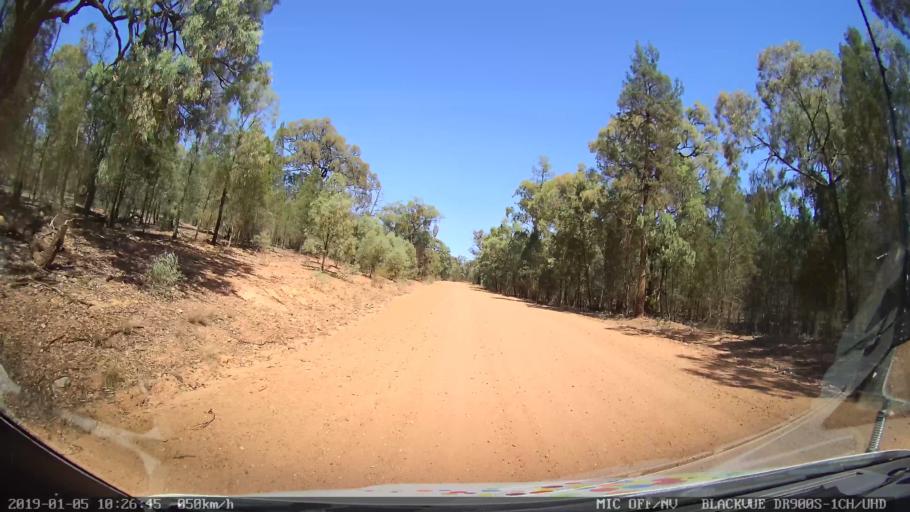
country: AU
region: New South Wales
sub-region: Gilgandra
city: Gilgandra
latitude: -31.5522
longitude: 148.9529
